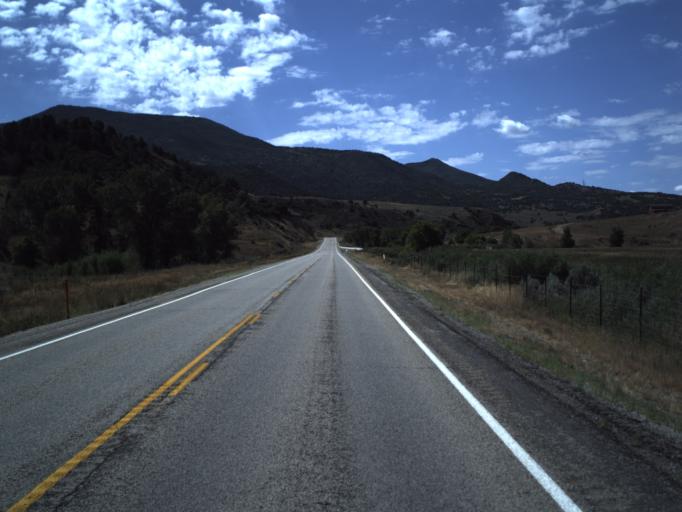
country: US
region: Utah
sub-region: Utah County
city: Woodland Hills
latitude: 39.9828
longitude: -111.5025
